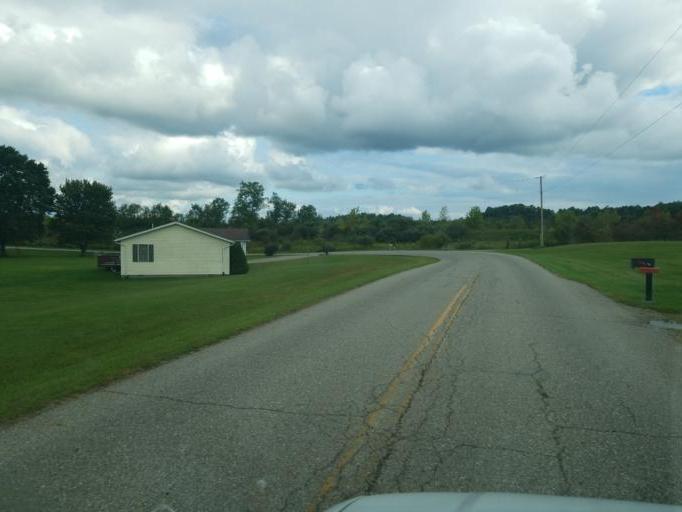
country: US
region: Ohio
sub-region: Jackson County
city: Oak Hill
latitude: 38.9367
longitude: -82.5773
